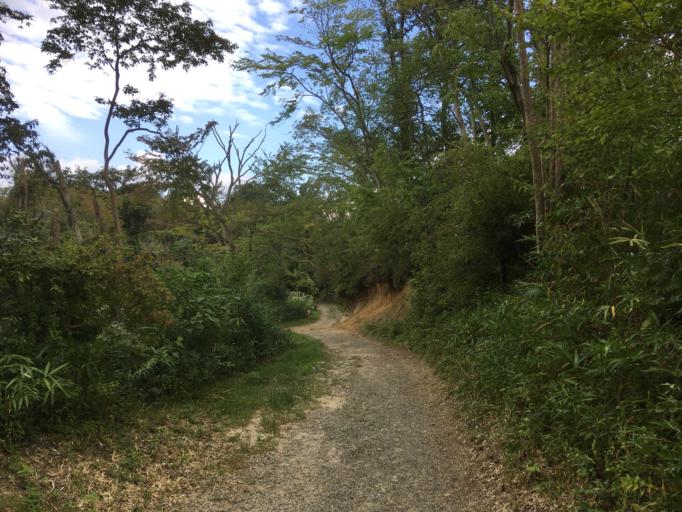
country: JP
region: Nara
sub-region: Ikoma-shi
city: Ikoma
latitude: 34.7246
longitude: 135.6704
